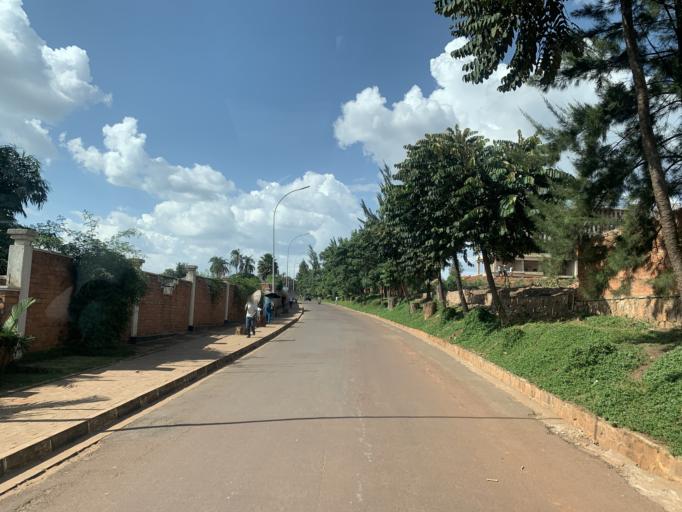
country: RW
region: Kigali
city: Kigali
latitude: -1.9602
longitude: 30.0606
